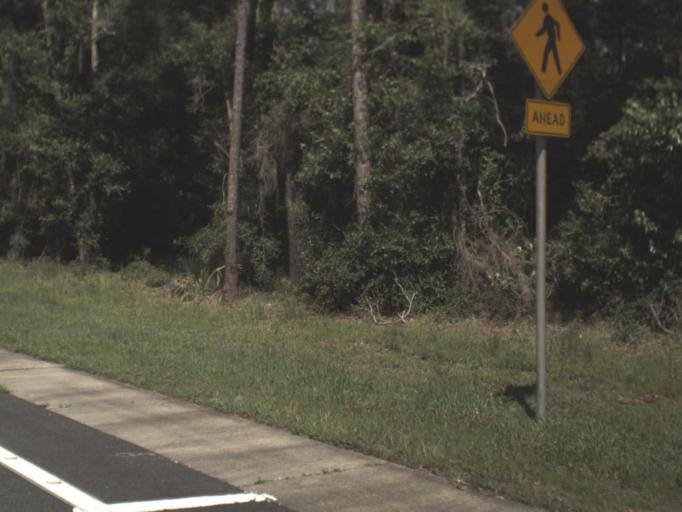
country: US
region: Florida
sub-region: Levy County
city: Chiefland
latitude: 29.3238
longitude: -82.7753
